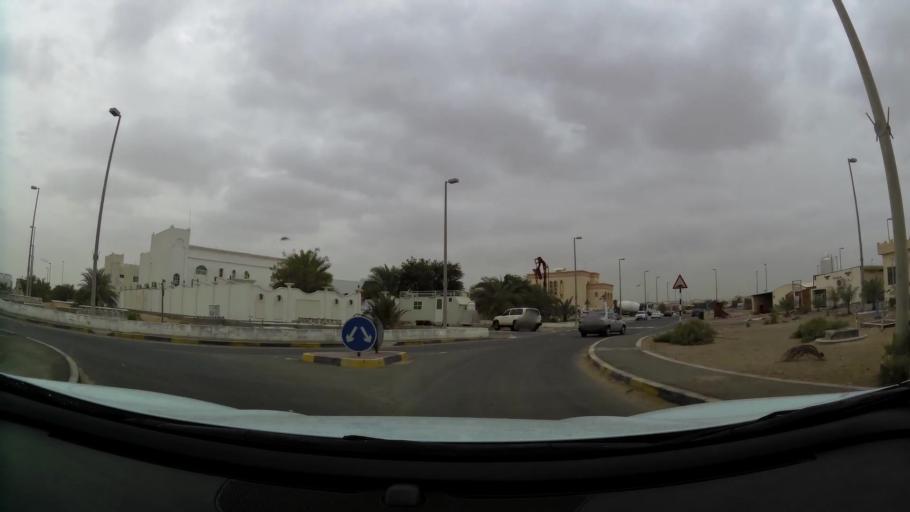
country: AE
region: Abu Dhabi
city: Abu Dhabi
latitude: 24.3308
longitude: 54.6368
